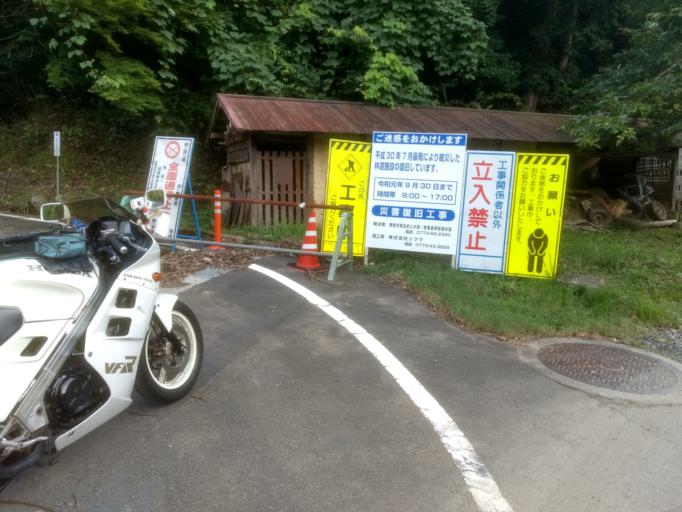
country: JP
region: Kyoto
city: Maizuru
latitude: 35.4009
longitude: 135.3495
